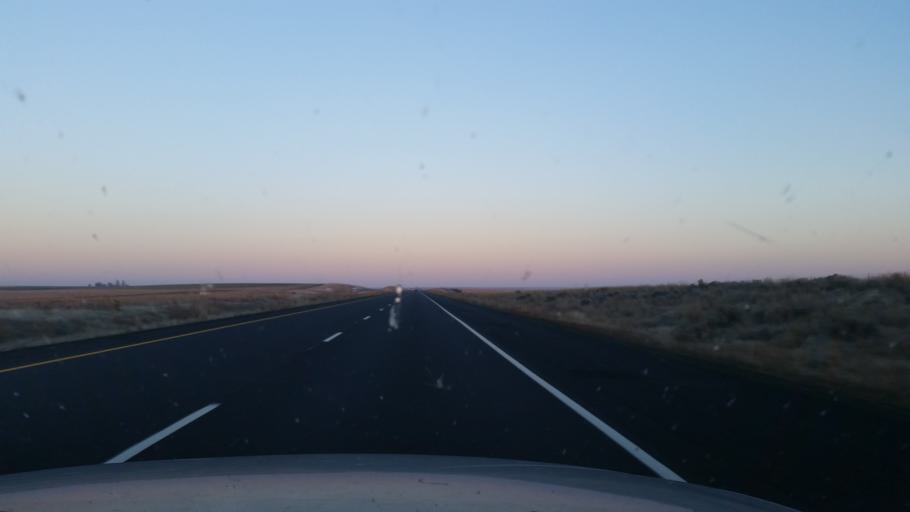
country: US
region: Washington
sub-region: Grant County
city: Warden
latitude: 47.0859
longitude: -118.7965
